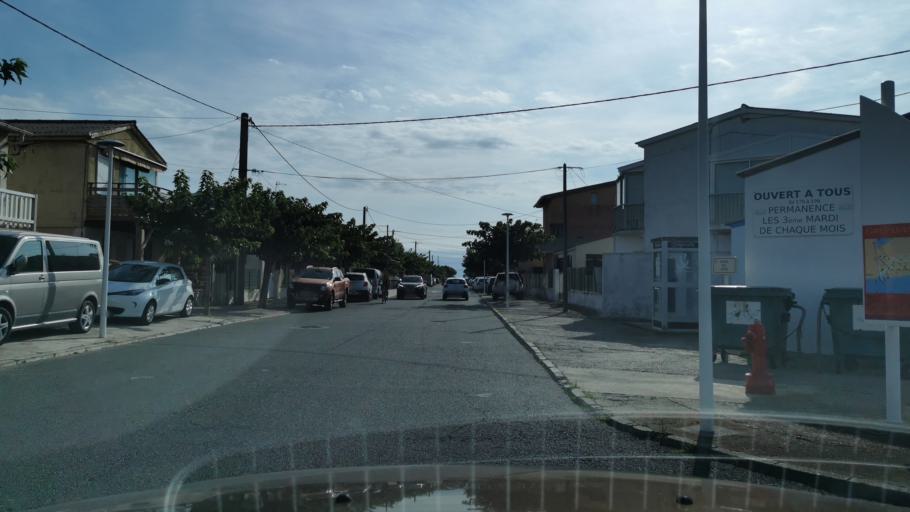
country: FR
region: Languedoc-Roussillon
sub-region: Departement de l'Aude
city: Gruissan
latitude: 43.0971
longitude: 3.1062
